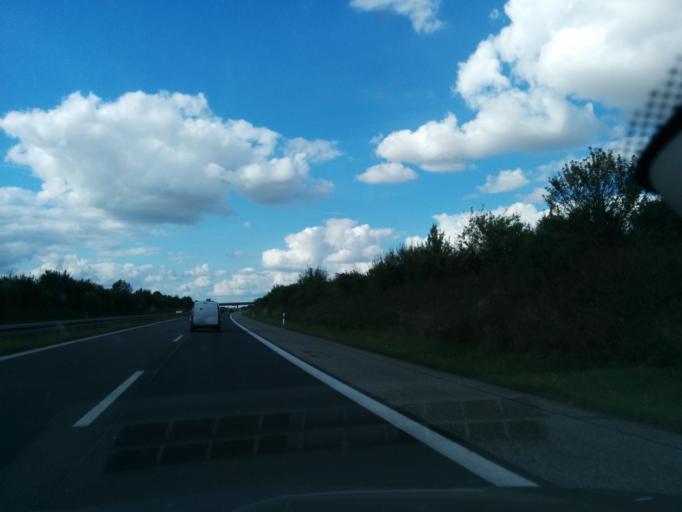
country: DE
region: Brandenburg
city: Gramzow
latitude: 53.2590
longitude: 14.0002
